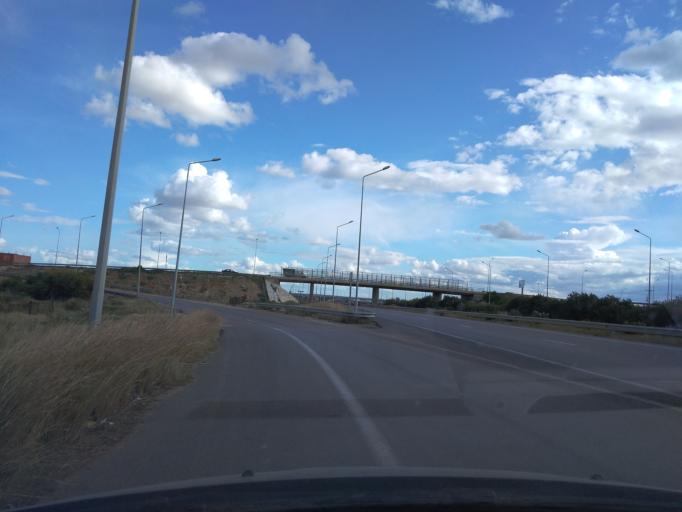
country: TN
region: Susah
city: Masakin
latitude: 35.7132
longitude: 10.5576
